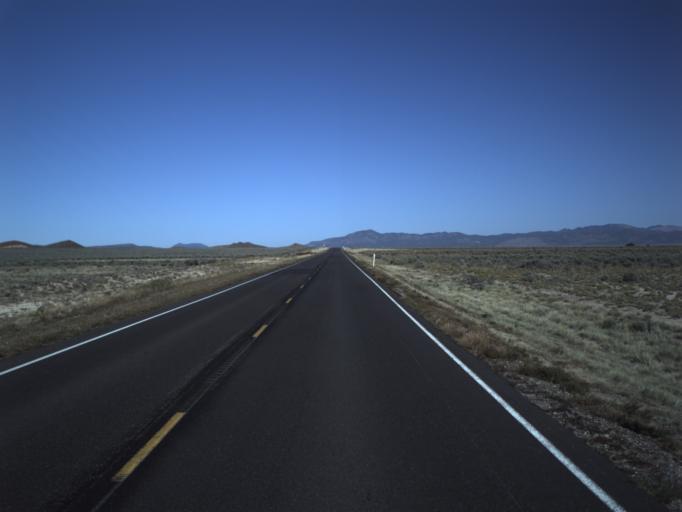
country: US
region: Utah
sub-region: Washington County
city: Enterprise
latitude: 37.7304
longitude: -113.7144
